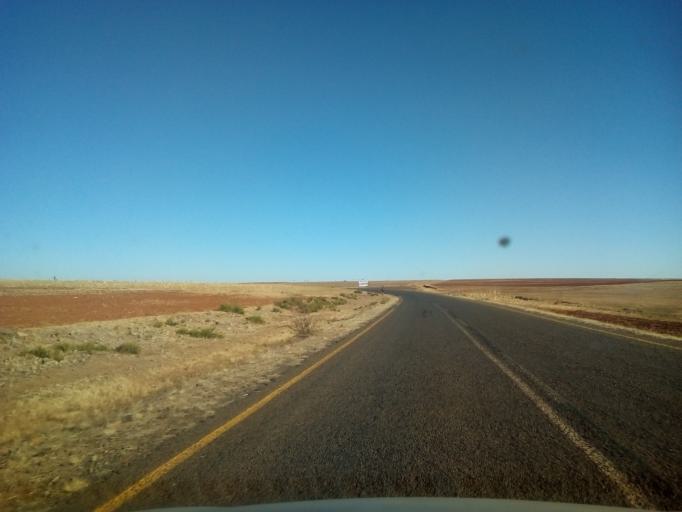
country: LS
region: Berea
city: Teyateyaneng
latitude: -29.2820
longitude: 27.6634
